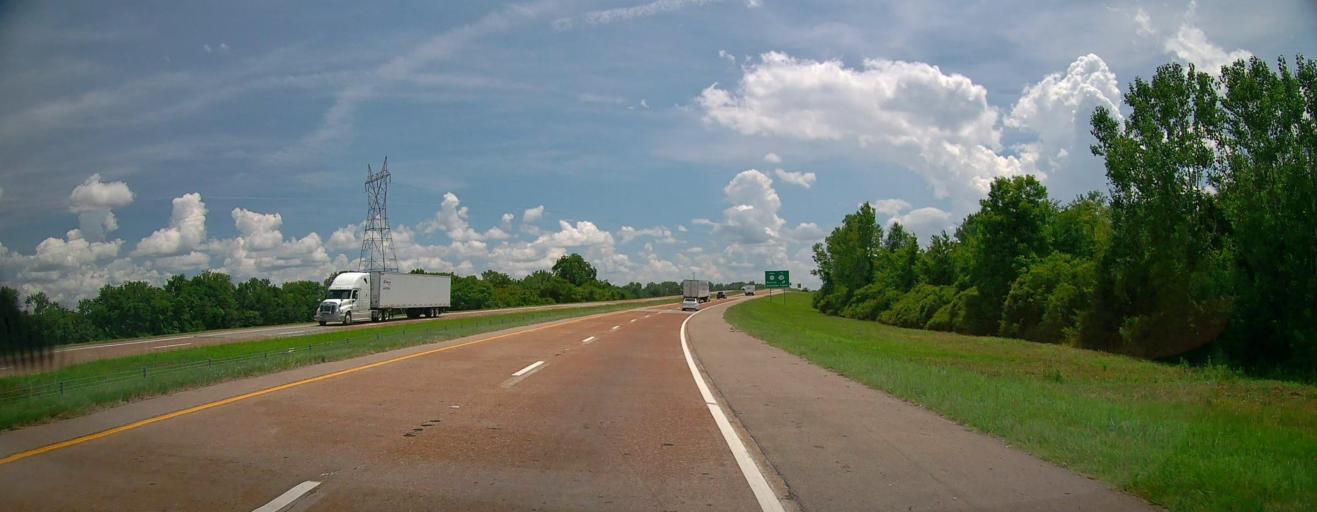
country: US
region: Mississippi
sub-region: Lee County
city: Tupelo
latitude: 34.2656
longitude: -88.6943
